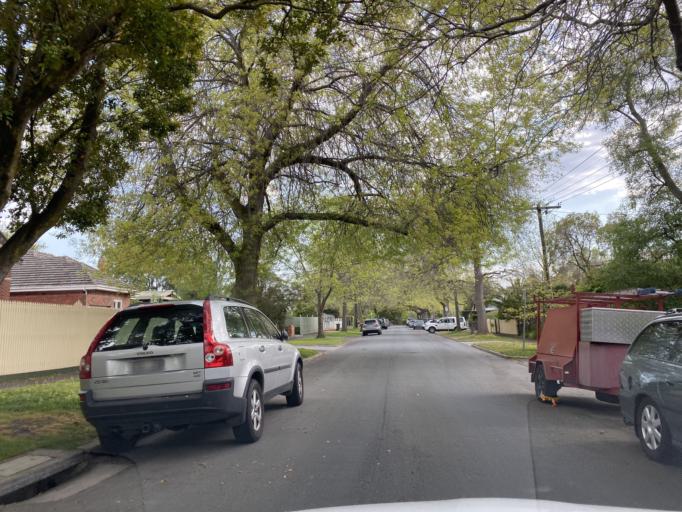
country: AU
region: Victoria
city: Balwyn
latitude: -37.8279
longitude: 145.0661
